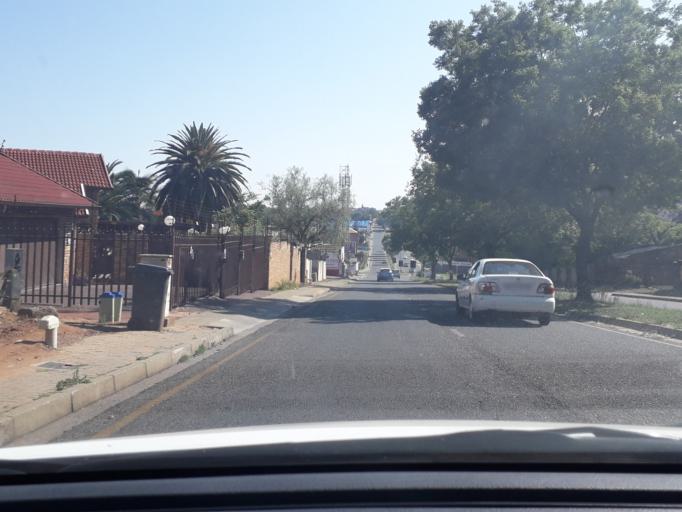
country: ZA
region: Gauteng
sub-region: City of Johannesburg Metropolitan Municipality
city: Roodepoort
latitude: -26.1086
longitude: 27.9742
